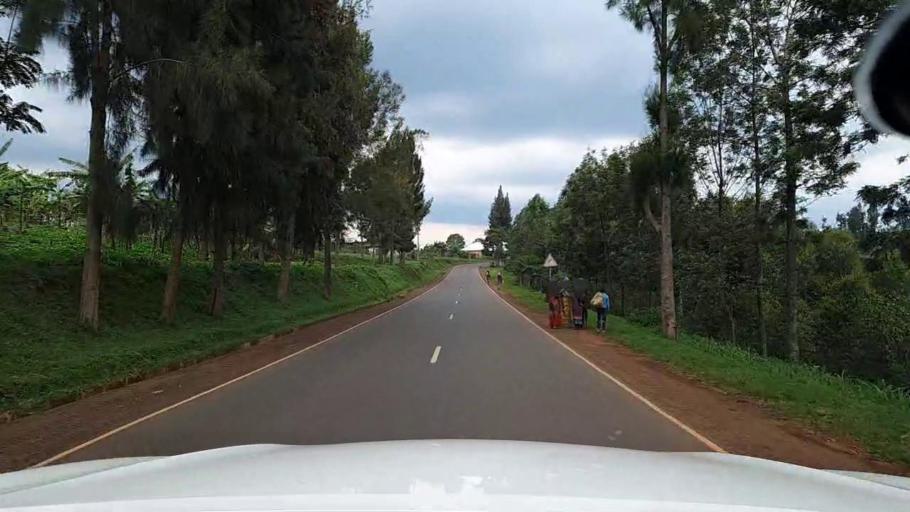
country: RW
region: Western Province
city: Cyangugu
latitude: -2.5940
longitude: 28.9281
